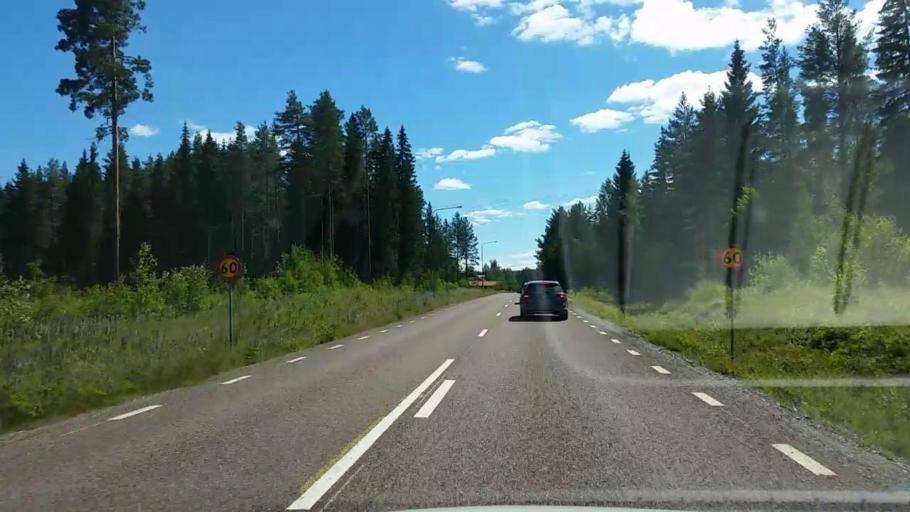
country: SE
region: Gaevleborg
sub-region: Ovanakers Kommun
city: Edsbyn
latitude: 61.2084
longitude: 15.8709
